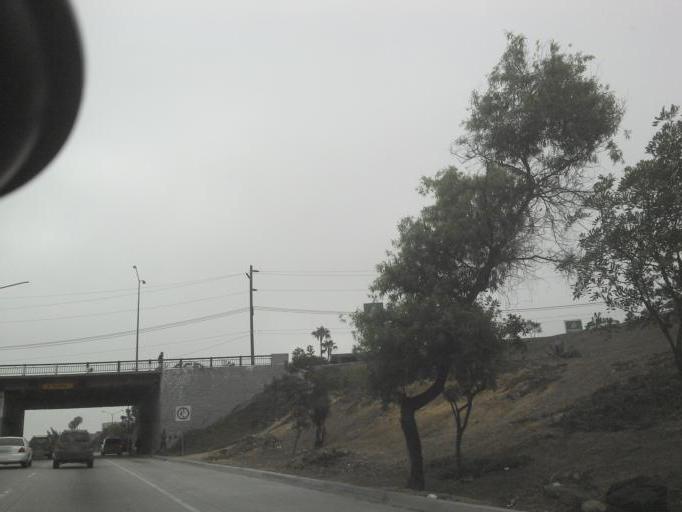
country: US
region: California
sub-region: San Diego County
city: Imperial Beach
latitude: 32.5306
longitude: -117.0737
